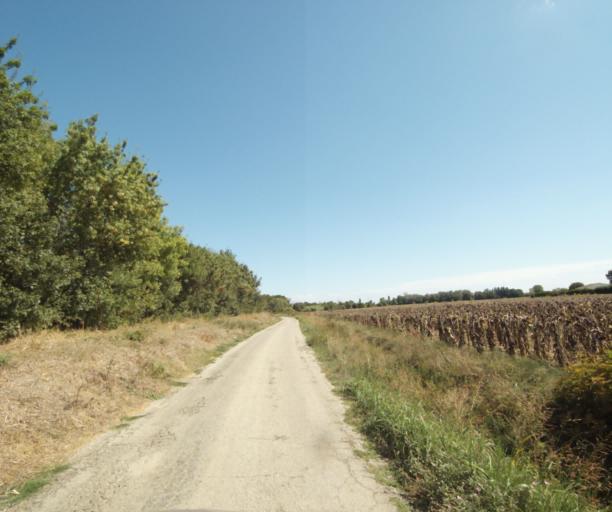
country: FR
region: Languedoc-Roussillon
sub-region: Departement du Gard
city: Rodilhan
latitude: 43.8162
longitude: 4.4026
